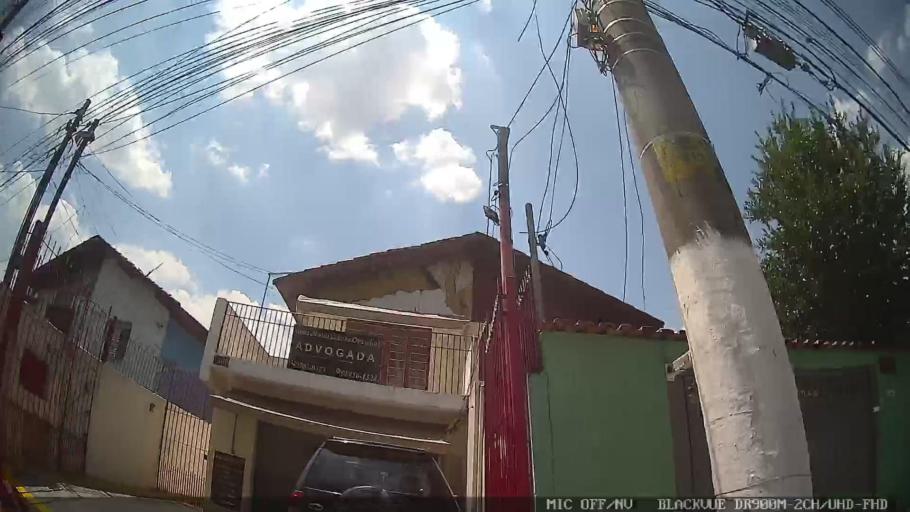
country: BR
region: Sao Paulo
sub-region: Taboao Da Serra
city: Taboao da Serra
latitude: -23.6493
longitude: -46.7510
